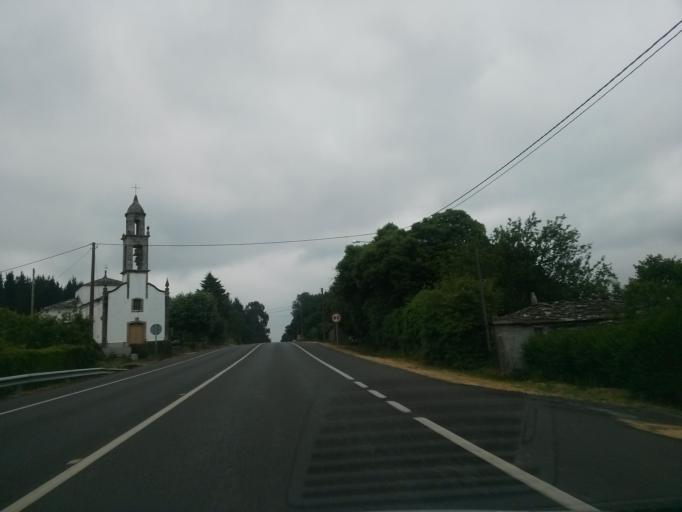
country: ES
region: Galicia
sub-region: Provincia de Lugo
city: Begonte
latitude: 43.1421
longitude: -7.6730
